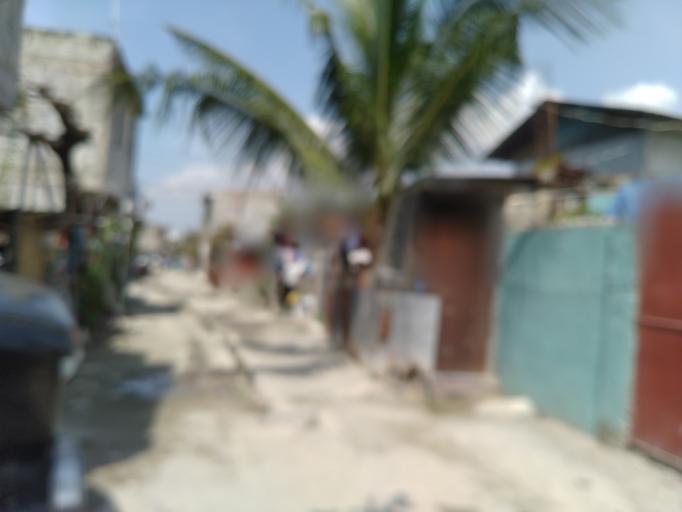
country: PH
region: Calabarzon
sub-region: Province of Rizal
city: Taytay
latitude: 14.5404
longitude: 121.1120
